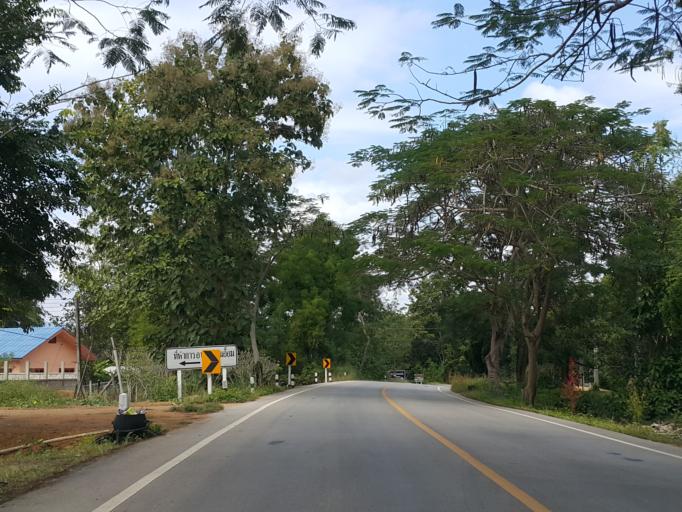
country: TH
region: Lampang
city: Hang Chat
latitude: 18.4231
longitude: 99.4446
